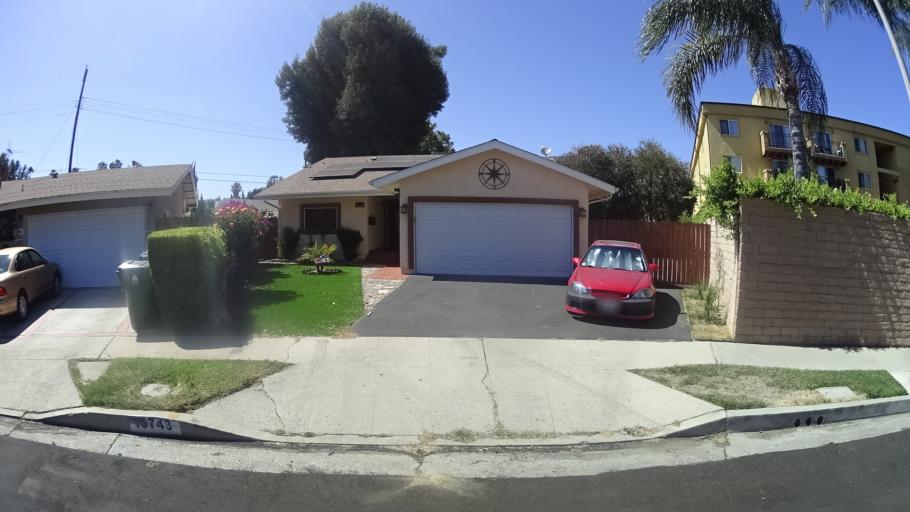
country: US
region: California
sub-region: Los Angeles County
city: Van Nuys
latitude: 34.1928
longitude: -118.4763
